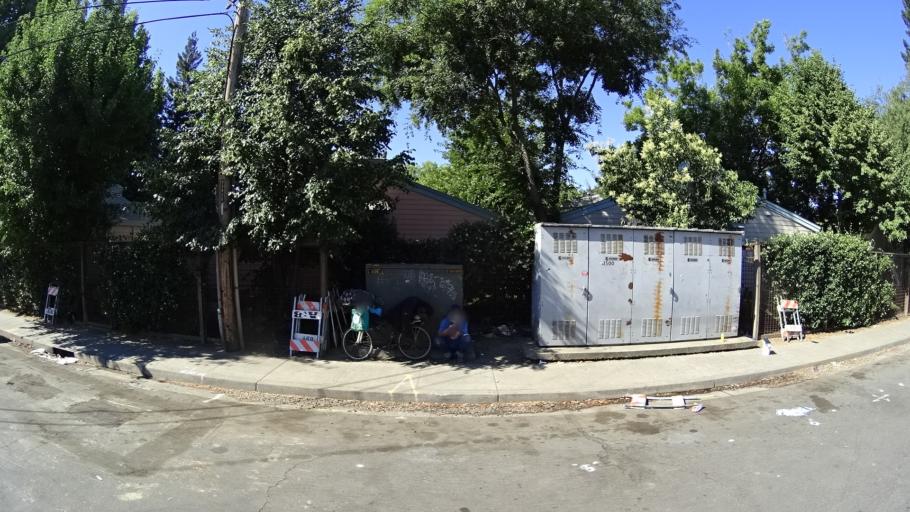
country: US
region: California
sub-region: Sacramento County
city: Sacramento
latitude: 38.5883
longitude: -121.4822
